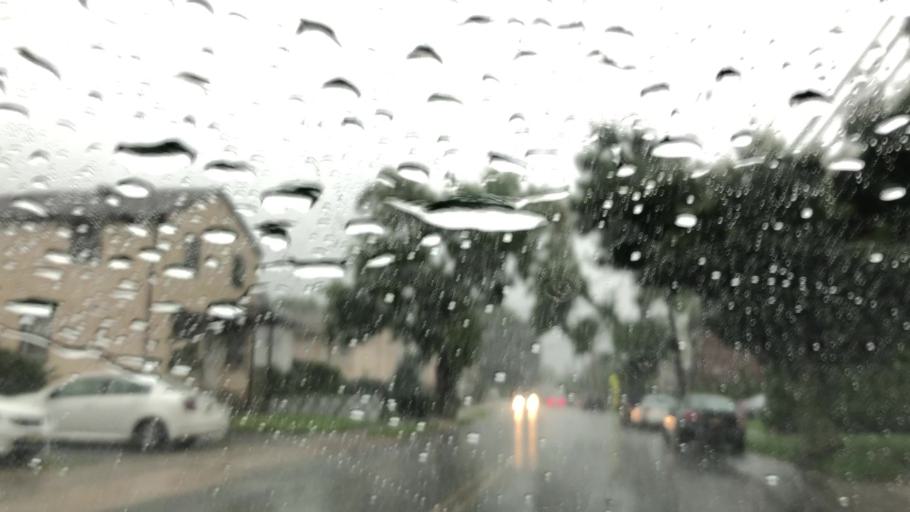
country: US
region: New Jersey
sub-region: Bergen County
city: Elmwood Park
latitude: 40.9088
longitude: -74.1138
